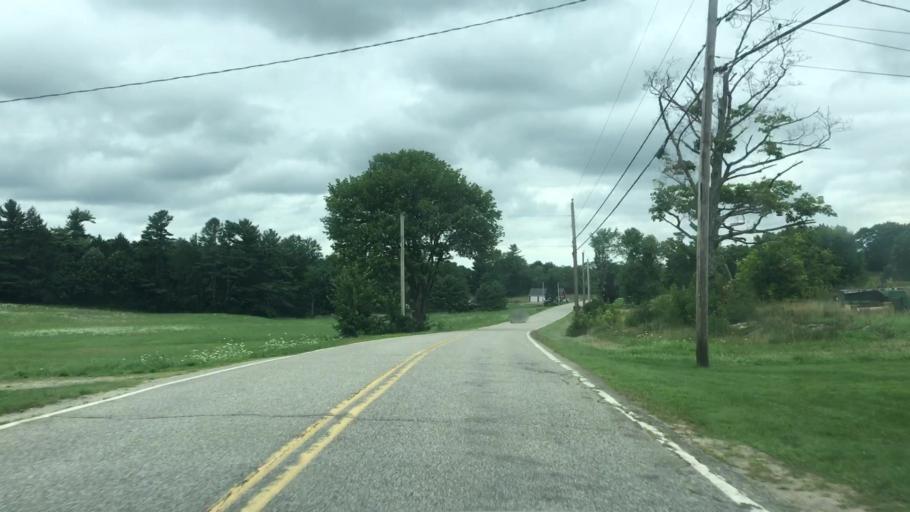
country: US
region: Maine
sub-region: York County
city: Biddeford
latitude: 43.5142
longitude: -70.5113
